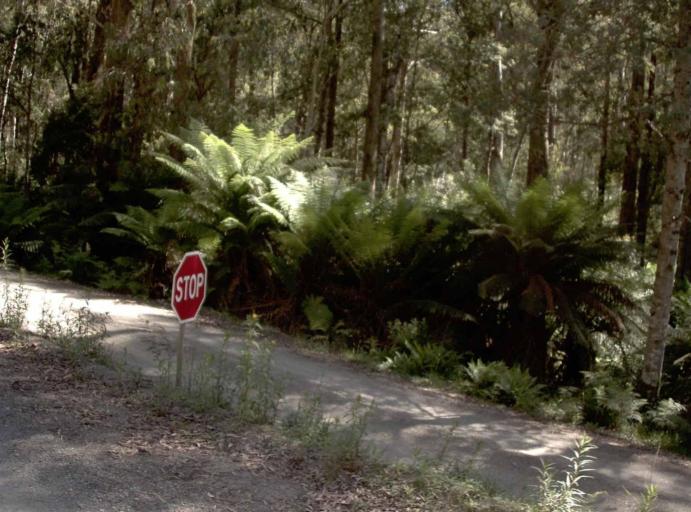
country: AU
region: New South Wales
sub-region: Bombala
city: Bombala
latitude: -37.2418
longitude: 148.7574
